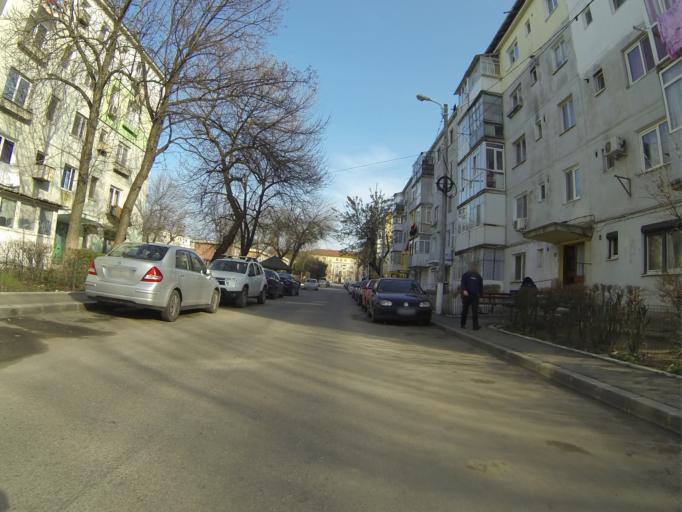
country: RO
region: Dolj
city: Craiova
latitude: 44.3047
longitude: 23.8166
